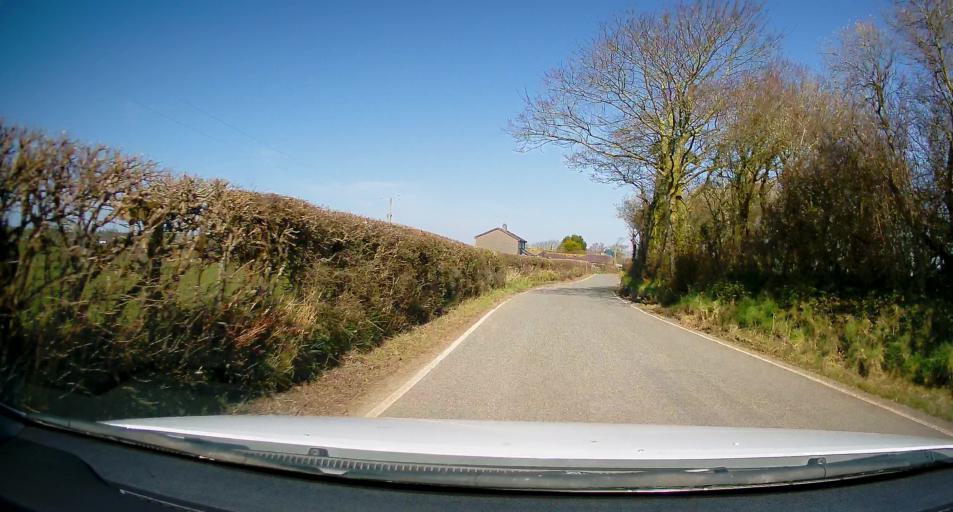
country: GB
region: Wales
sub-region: County of Ceredigion
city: Lledrod
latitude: 52.3048
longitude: -4.0670
